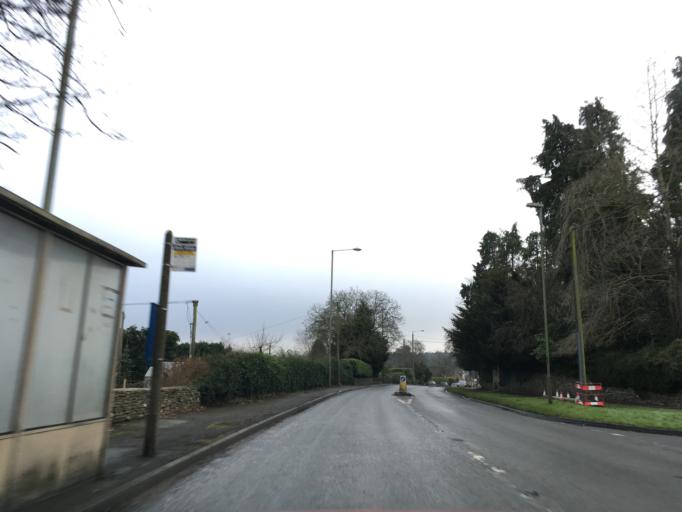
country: GB
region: England
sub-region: Gloucestershire
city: Cirencester
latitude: 51.7305
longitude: -1.9737
